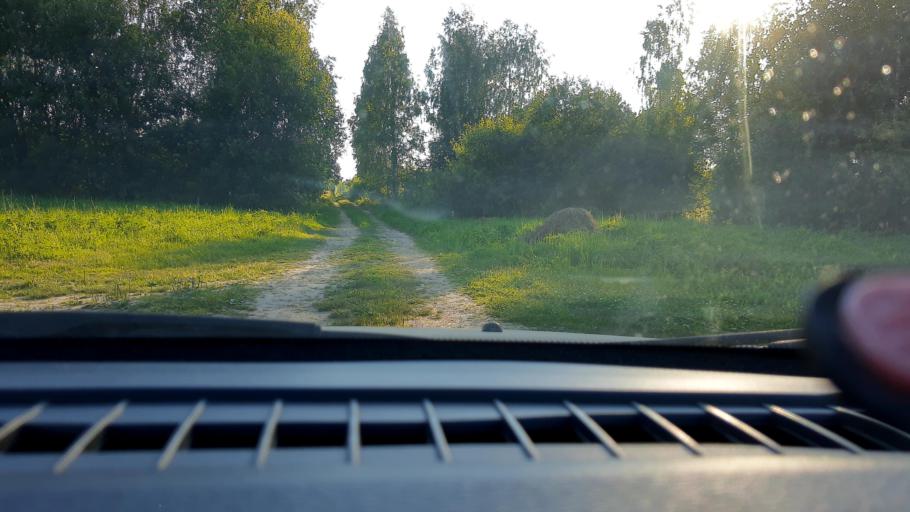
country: RU
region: Nizjnij Novgorod
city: Burevestnik
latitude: 56.0464
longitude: 43.8772
